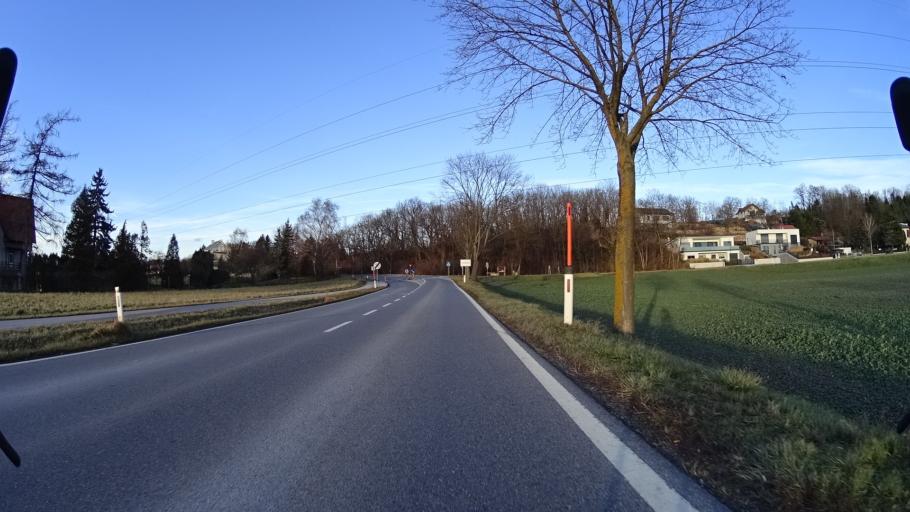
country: AT
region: Lower Austria
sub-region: Politischer Bezirk Korneuburg
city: Leobendorf
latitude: 48.3755
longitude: 16.2934
